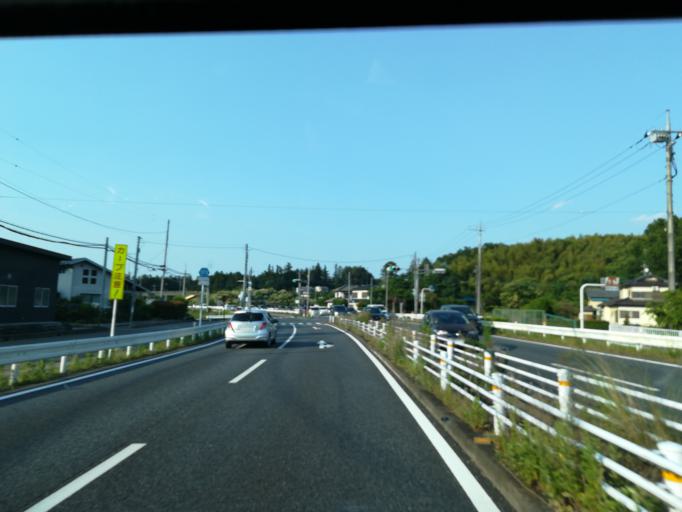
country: JP
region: Saitama
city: Kumagaya
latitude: 36.0849
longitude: 139.3597
